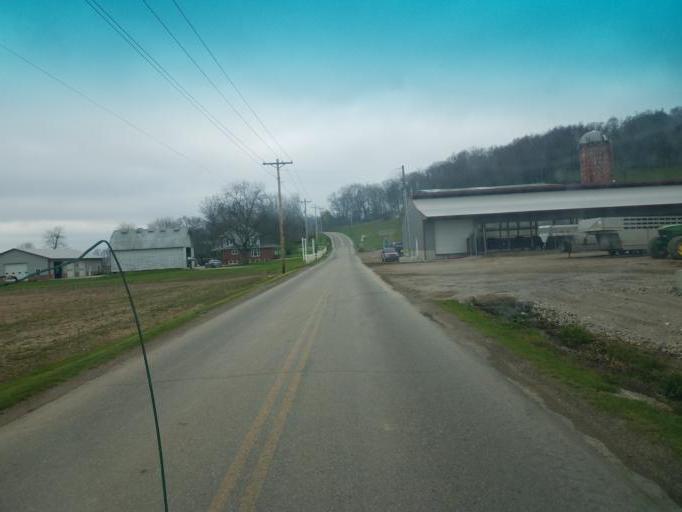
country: US
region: Ohio
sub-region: Stark County
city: Beach City
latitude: 40.6049
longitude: -81.6622
